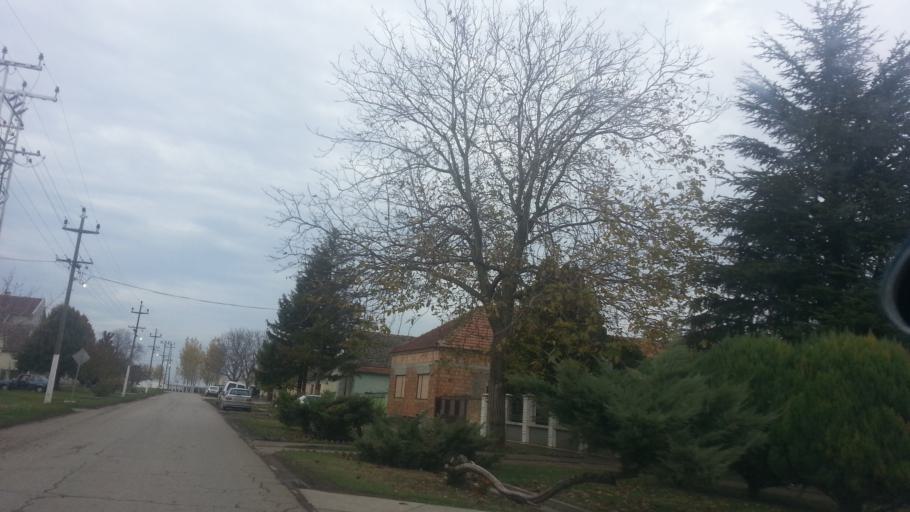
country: RS
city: Golubinci
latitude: 44.9962
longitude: 20.0610
